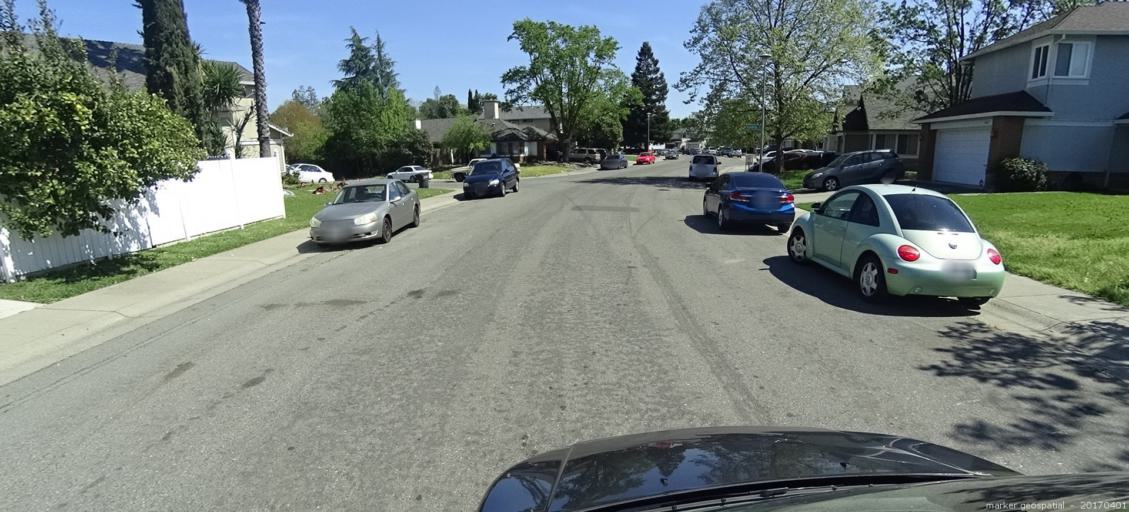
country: US
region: California
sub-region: Sacramento County
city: Laguna
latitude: 38.4462
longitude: -121.4334
